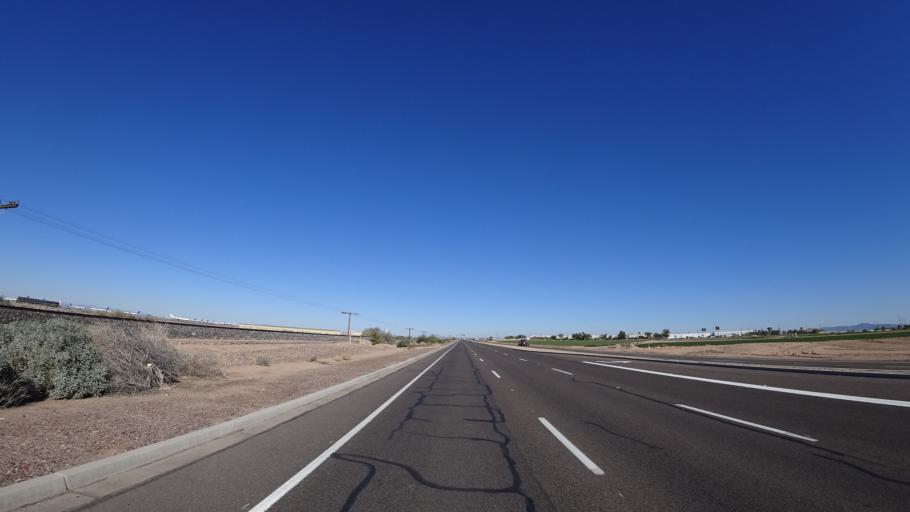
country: US
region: Arizona
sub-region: Maricopa County
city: Goodyear
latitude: 33.4117
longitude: -112.3811
